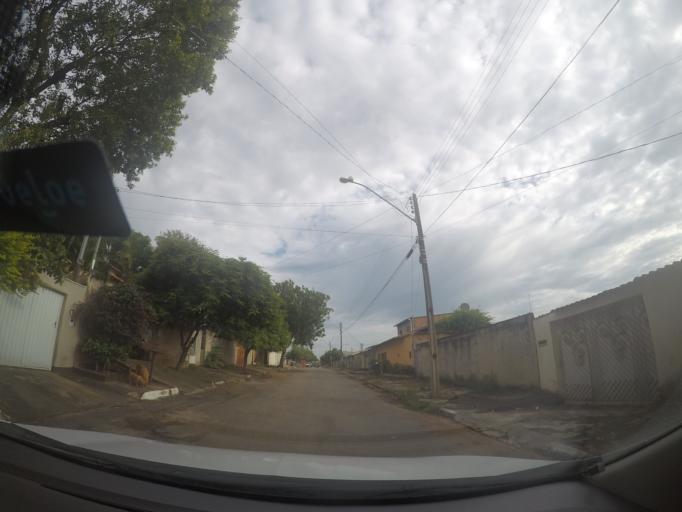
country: BR
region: Goias
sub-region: Goiania
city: Goiania
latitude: -16.6878
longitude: -49.1986
